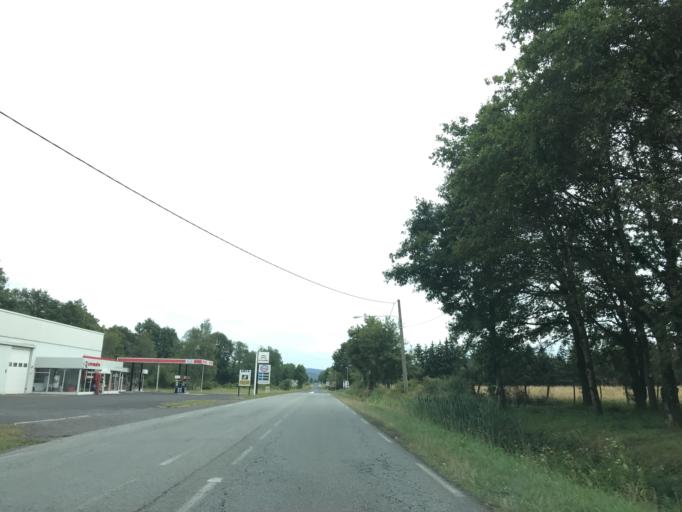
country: FR
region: Auvergne
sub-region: Departement du Puy-de-Dome
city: Peschadoires
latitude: 45.7938
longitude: 3.5244
